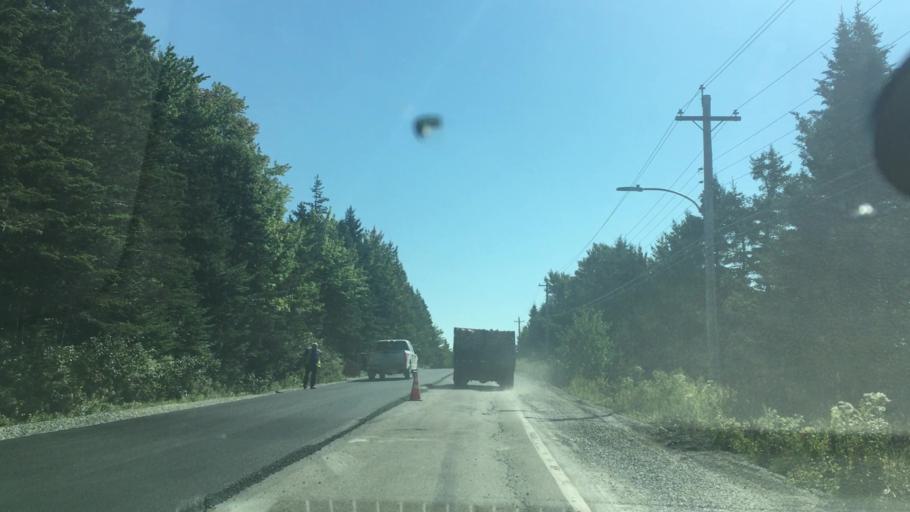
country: CA
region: Nova Scotia
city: New Glasgow
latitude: 44.9095
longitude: -62.5023
